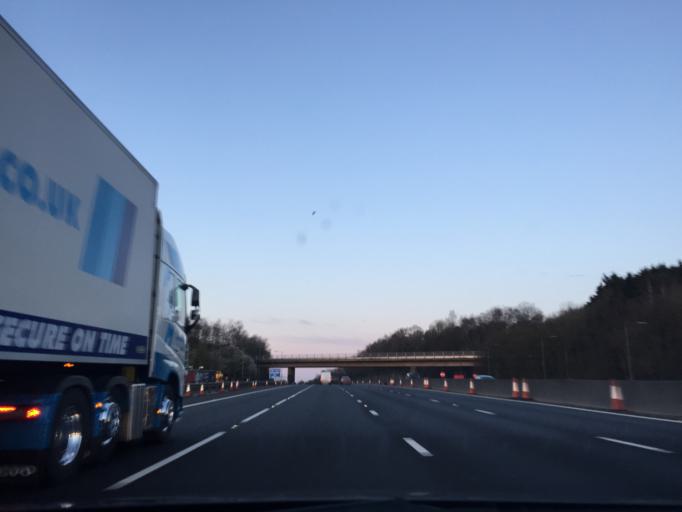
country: GB
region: England
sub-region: Hampshire
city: Totton
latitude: 50.9570
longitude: -1.4491
